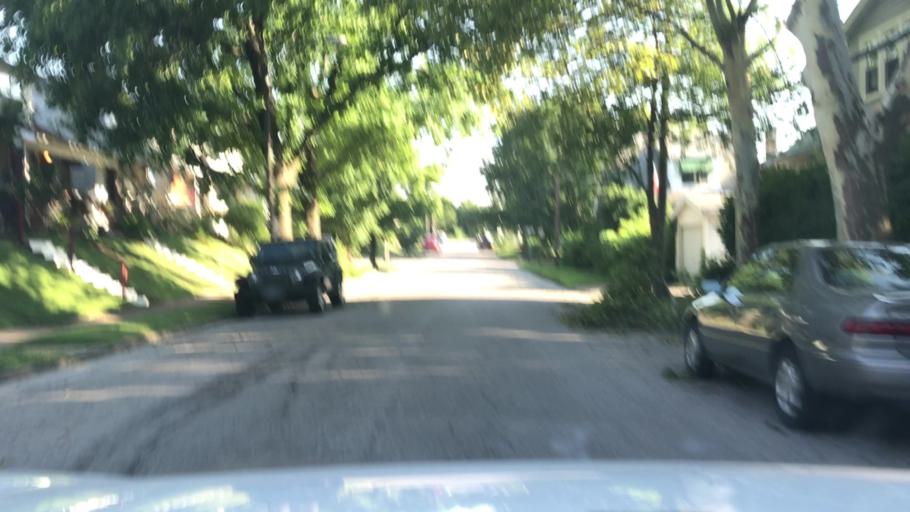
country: US
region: Missouri
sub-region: Saint Louis County
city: Maplewood
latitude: 38.6107
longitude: -90.2926
